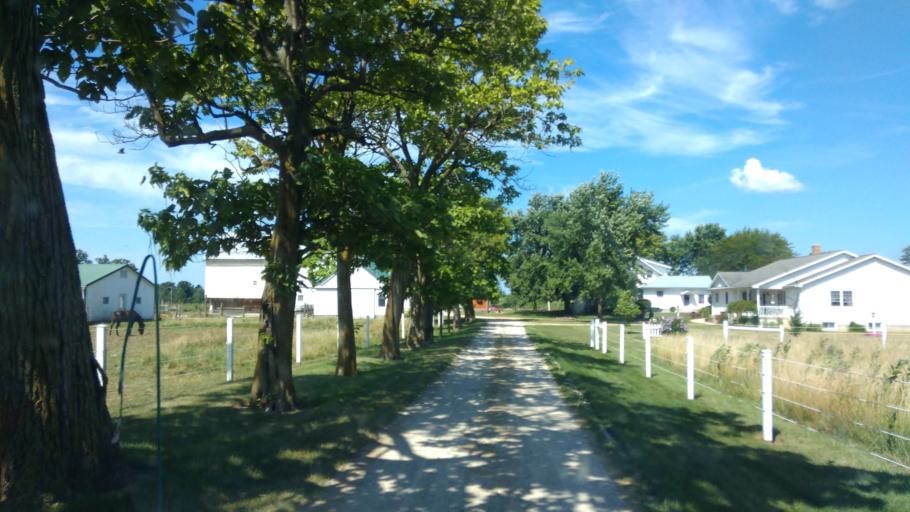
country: US
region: Indiana
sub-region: Adams County
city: Berne
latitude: 40.7026
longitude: -84.9757
